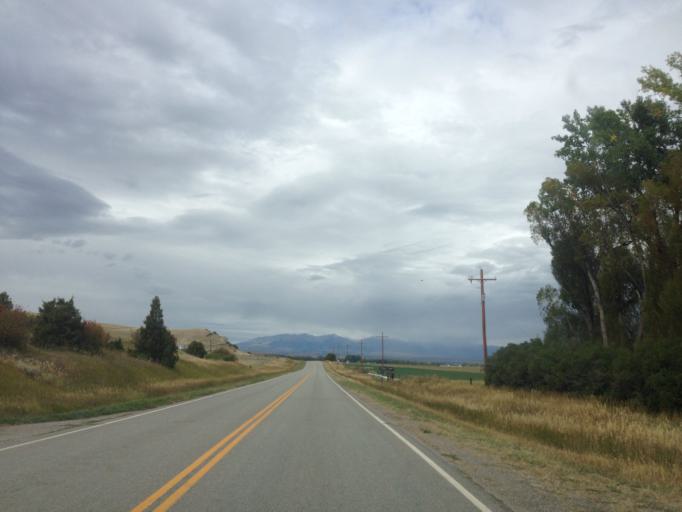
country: US
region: Montana
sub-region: Sweet Grass County
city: Big Timber
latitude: 45.7761
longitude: -109.8068
